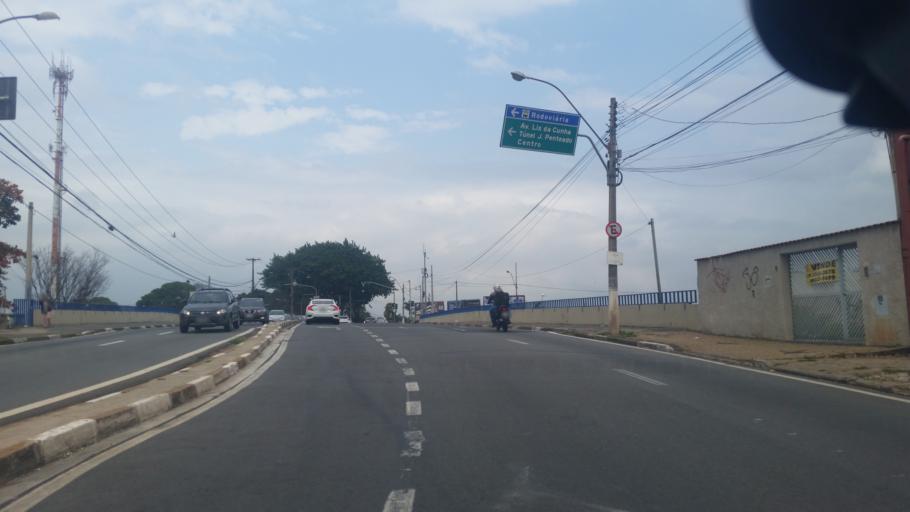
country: BR
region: Sao Paulo
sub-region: Campinas
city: Campinas
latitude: -22.9008
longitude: -47.0823
